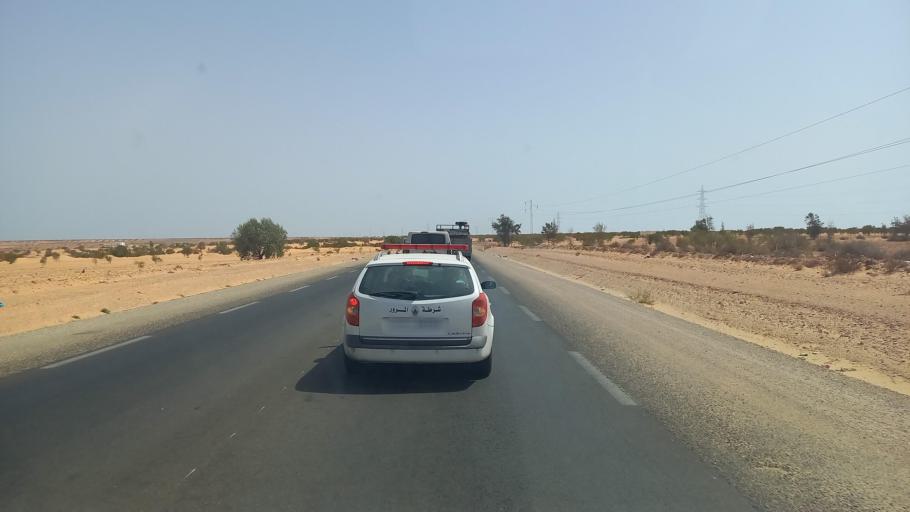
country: TN
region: Madanin
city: Zarzis
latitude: 33.4012
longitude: 10.8405
